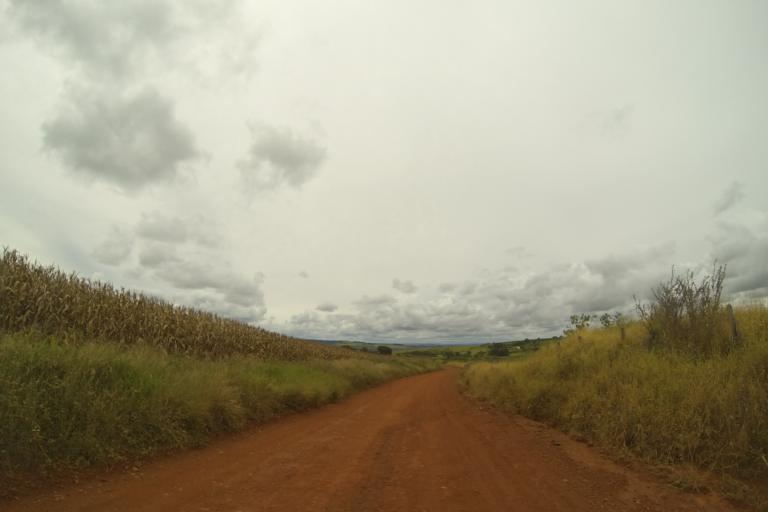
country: BR
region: Minas Gerais
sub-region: Ibia
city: Ibia
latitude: -19.6175
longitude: -46.6687
